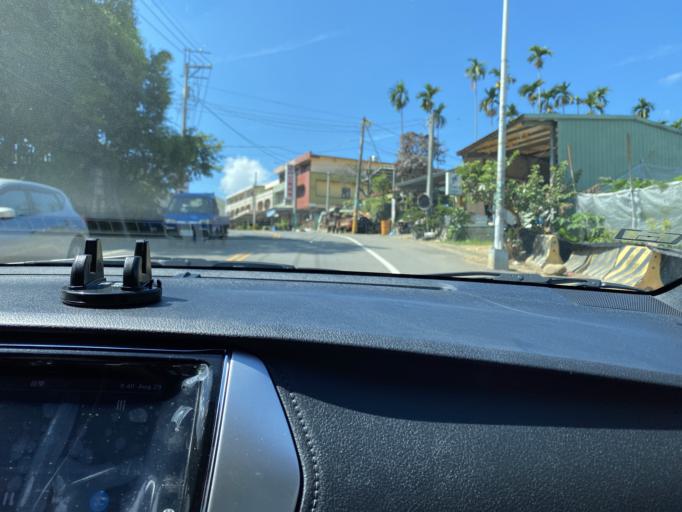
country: TW
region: Taiwan
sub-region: Nantou
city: Nantou
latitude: 23.8568
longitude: 120.6291
